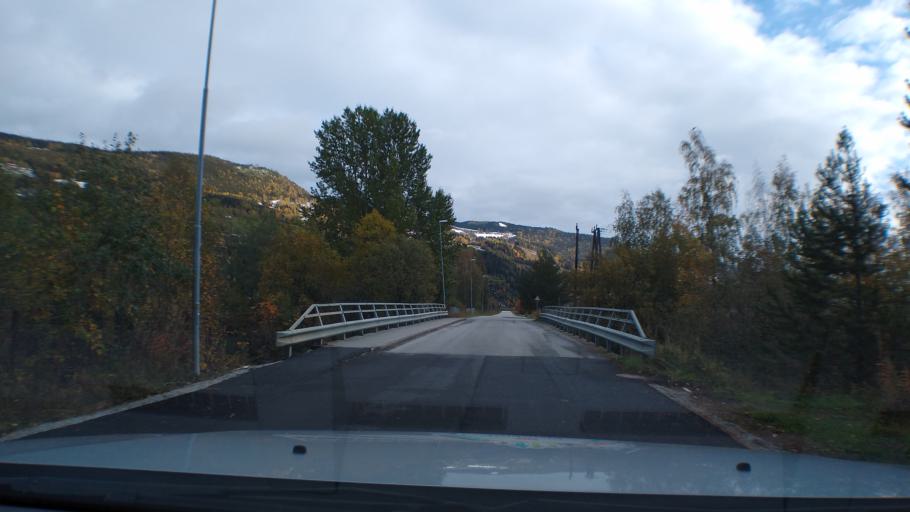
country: NO
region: Oppland
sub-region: Ringebu
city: Ringebu
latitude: 61.5264
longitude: 10.1411
